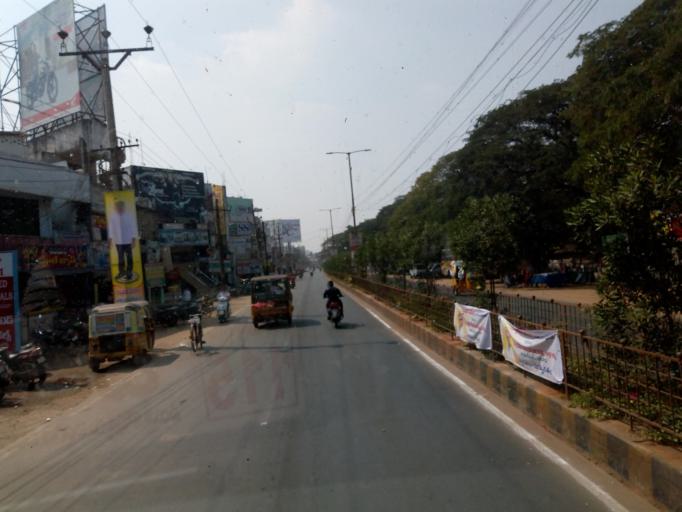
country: IN
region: Andhra Pradesh
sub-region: West Godavari
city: Eluru
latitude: 16.7098
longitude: 81.0928
